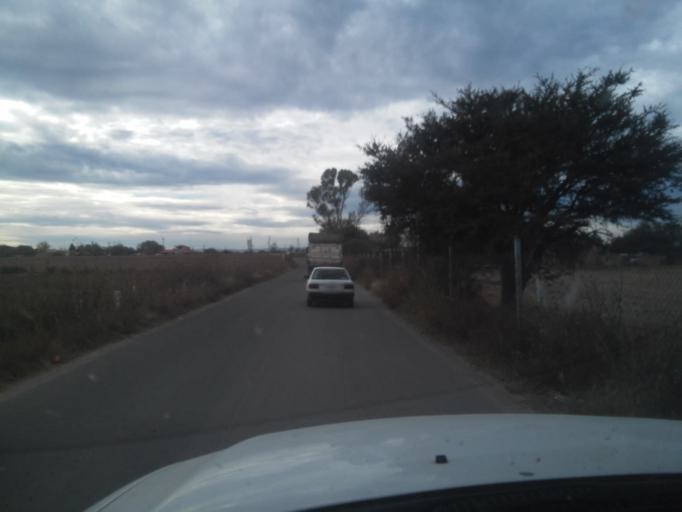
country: MX
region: Durango
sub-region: Durango
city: Jose Refugio Salcido
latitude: 24.0301
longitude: -104.5681
